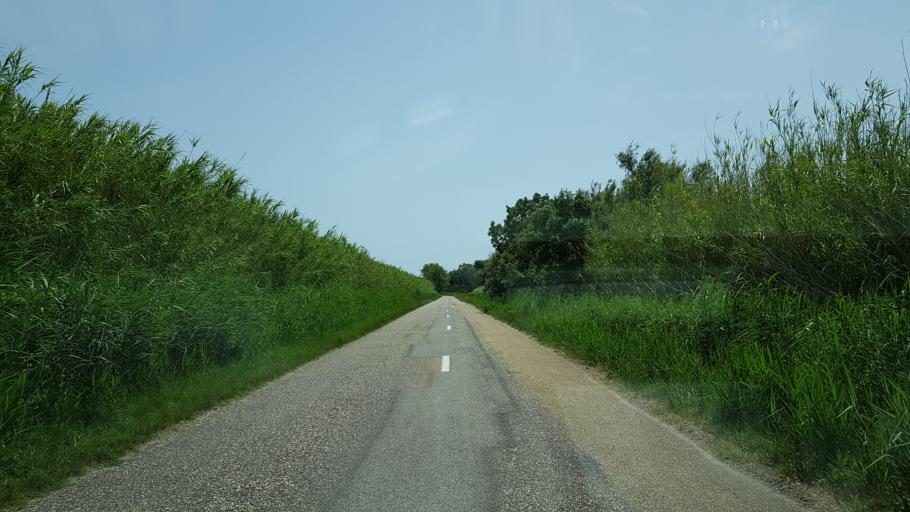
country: FR
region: Provence-Alpes-Cote d'Azur
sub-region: Departement des Bouches-du-Rhone
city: Port-Saint-Louis-du-Rhone
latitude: 43.4543
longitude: 4.6590
